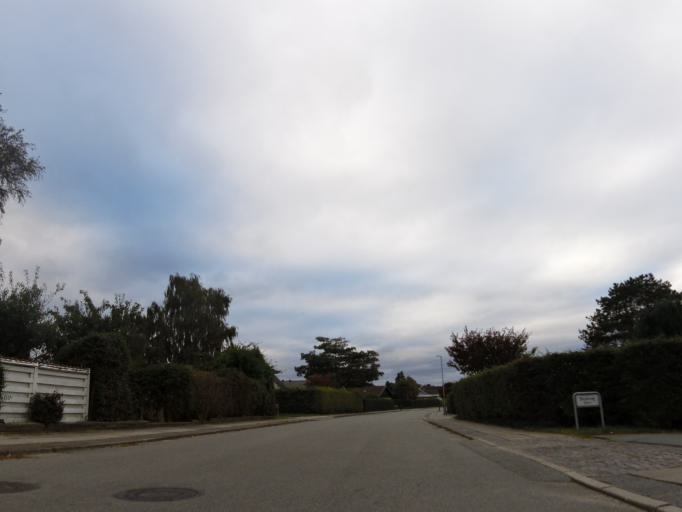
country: DK
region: Central Jutland
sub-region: Arhus Kommune
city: Hjortshoj
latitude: 56.2098
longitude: 10.2809
